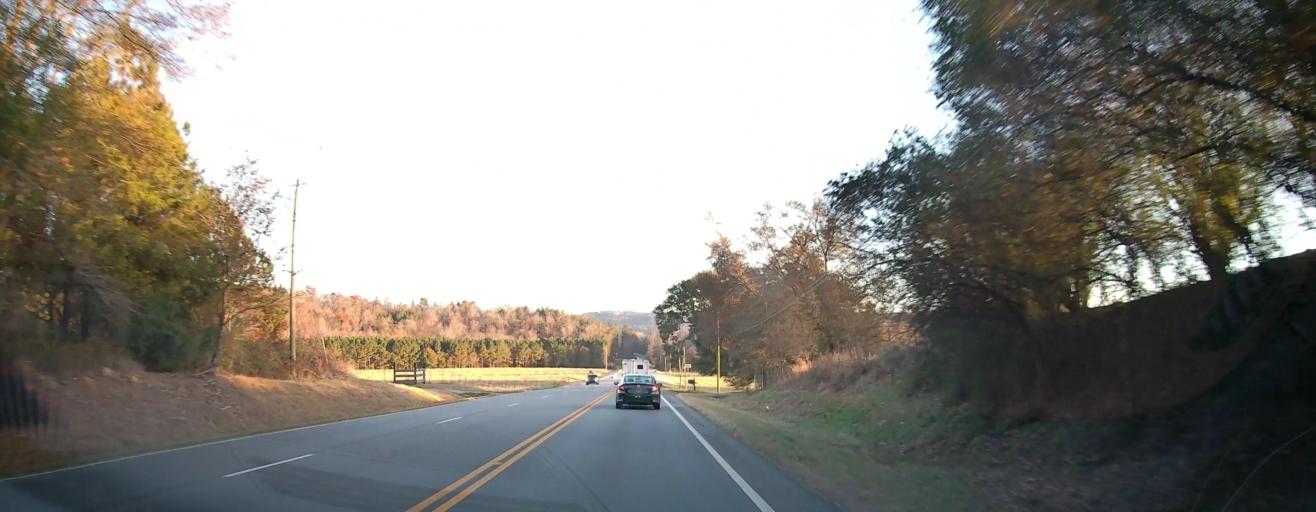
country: US
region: Alabama
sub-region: Etowah County
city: Attalla
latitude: 34.0495
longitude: -86.1596
